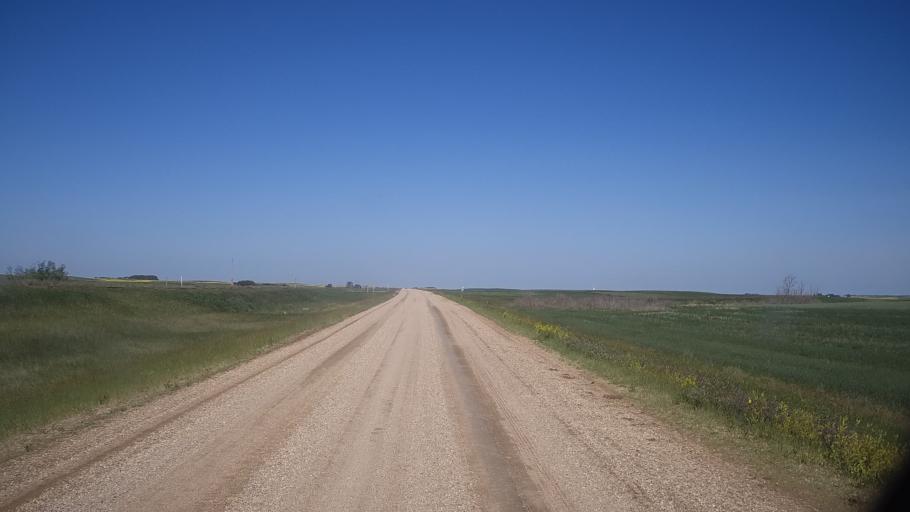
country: CA
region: Saskatchewan
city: Watrous
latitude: 51.8460
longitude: -105.9215
